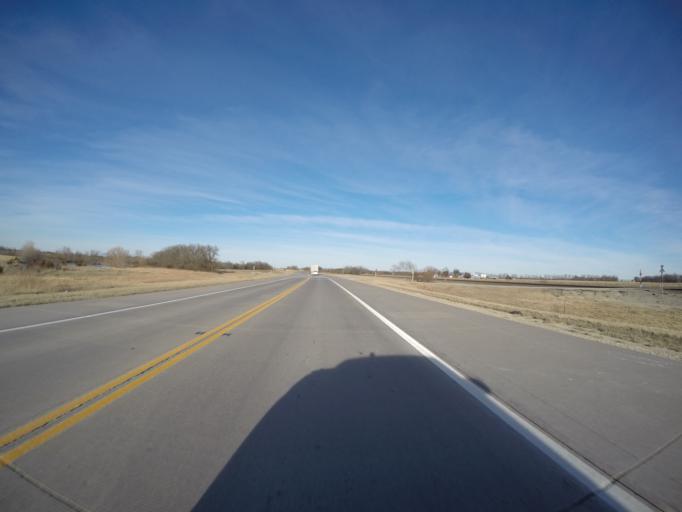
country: US
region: Kansas
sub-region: Harvey County
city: North Newton
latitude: 38.0732
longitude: -97.3007
